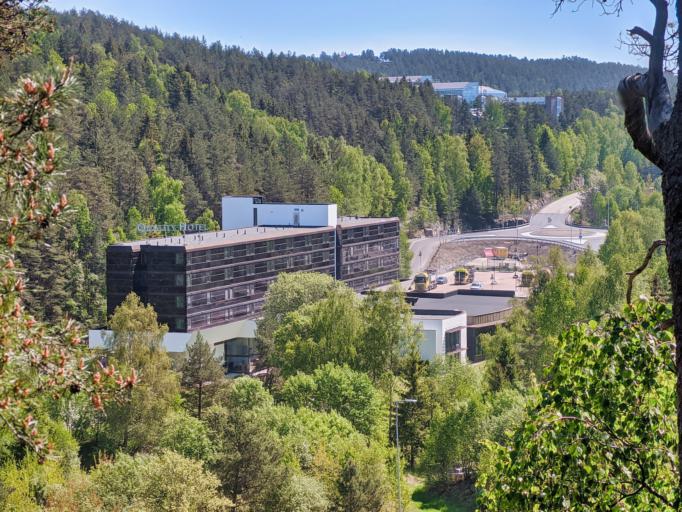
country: NO
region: Akershus
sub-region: Oppegard
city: Kolbotn
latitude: 59.8266
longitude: 10.7758
